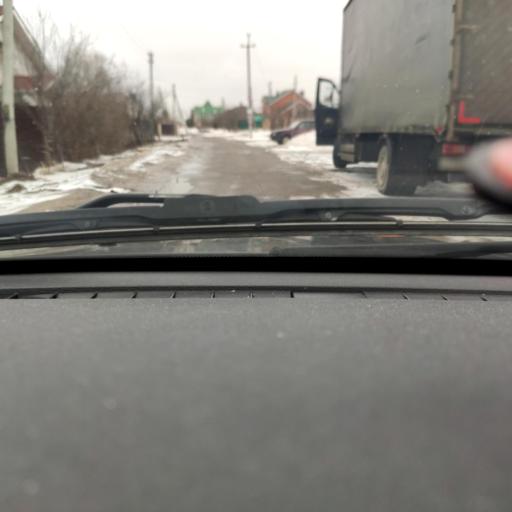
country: RU
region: Voronezj
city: Ramon'
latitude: 51.8204
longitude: 39.2690
